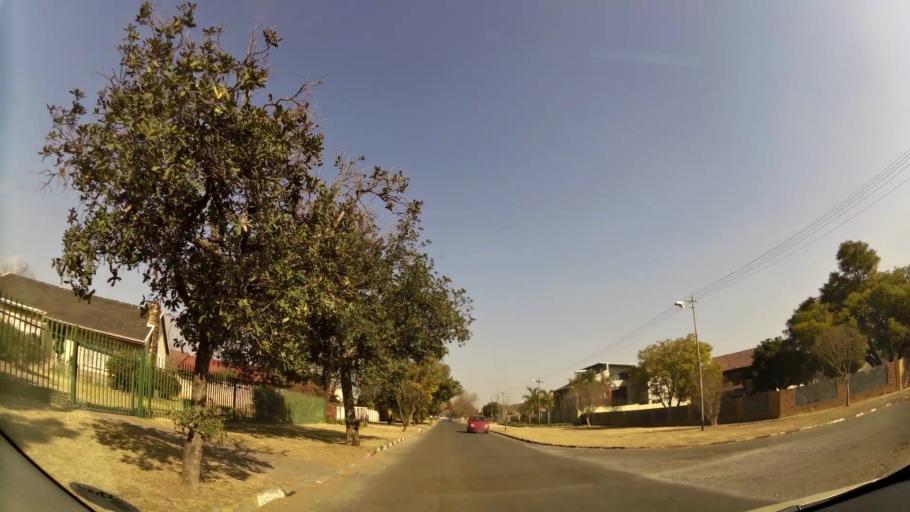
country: ZA
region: Gauteng
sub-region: West Rand District Municipality
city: Randfontein
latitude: -26.1626
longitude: 27.6989
